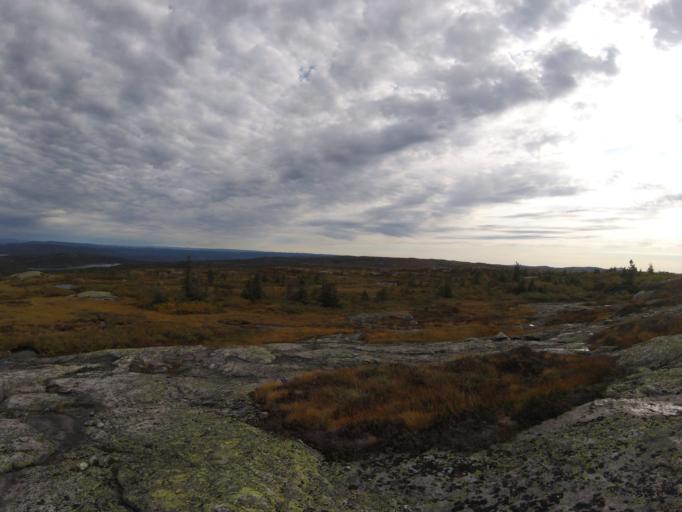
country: NO
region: Buskerud
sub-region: Rollag
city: Rollag
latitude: 59.8081
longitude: 9.3095
